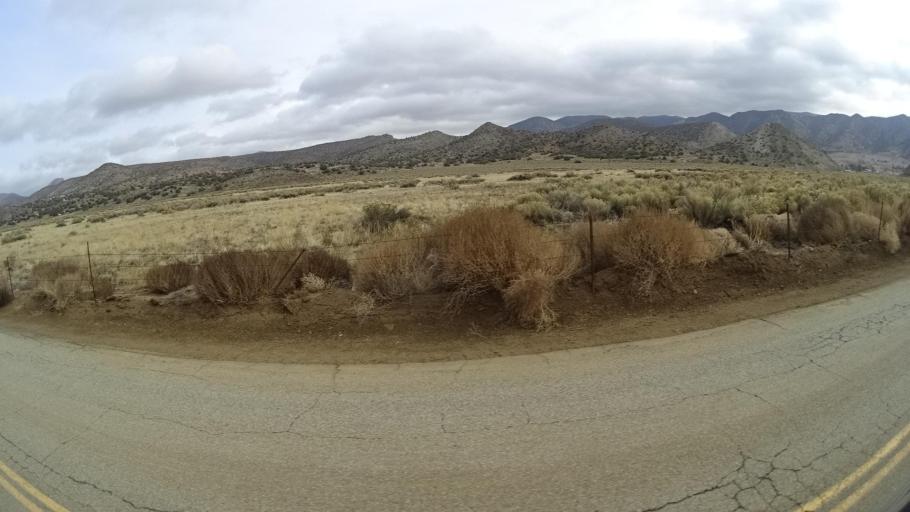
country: US
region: California
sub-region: Kern County
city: Tehachapi
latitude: 35.1547
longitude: -118.3213
